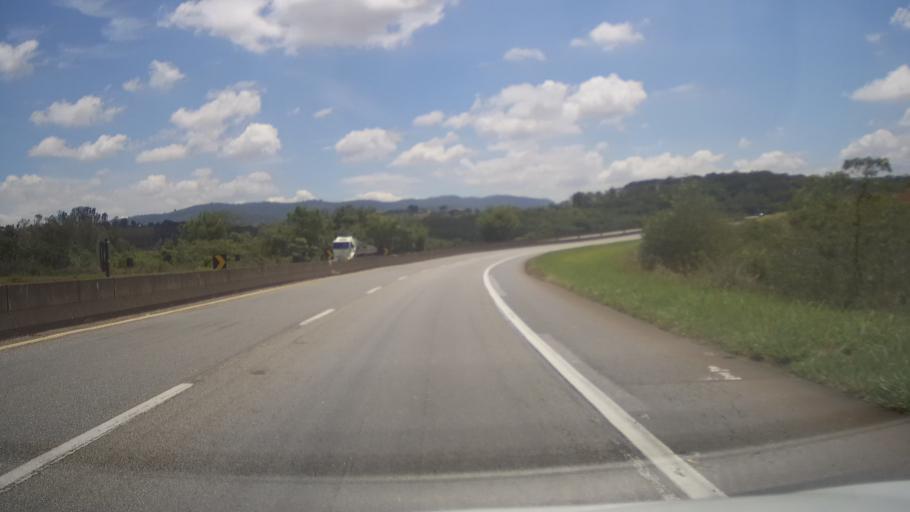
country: BR
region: Minas Gerais
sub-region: Sao Goncalo Do Sapucai
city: Sao Goncalo do Sapucai
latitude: -21.9234
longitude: -45.6122
